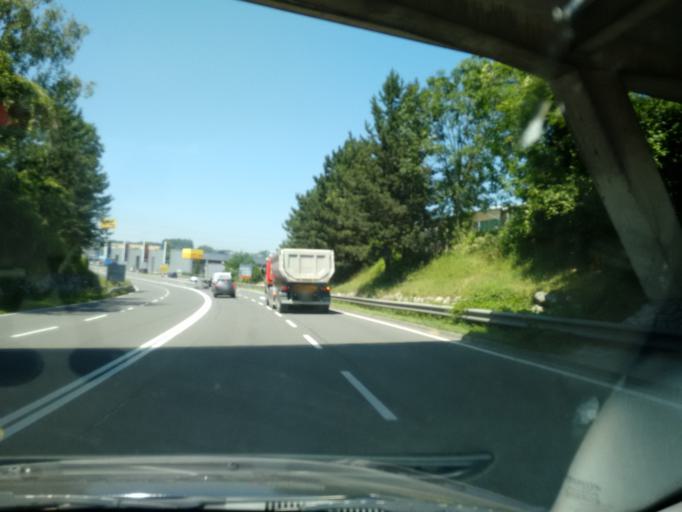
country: AT
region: Upper Austria
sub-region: Politischer Bezirk Gmunden
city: Gmunden
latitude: 47.9303
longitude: 13.7880
